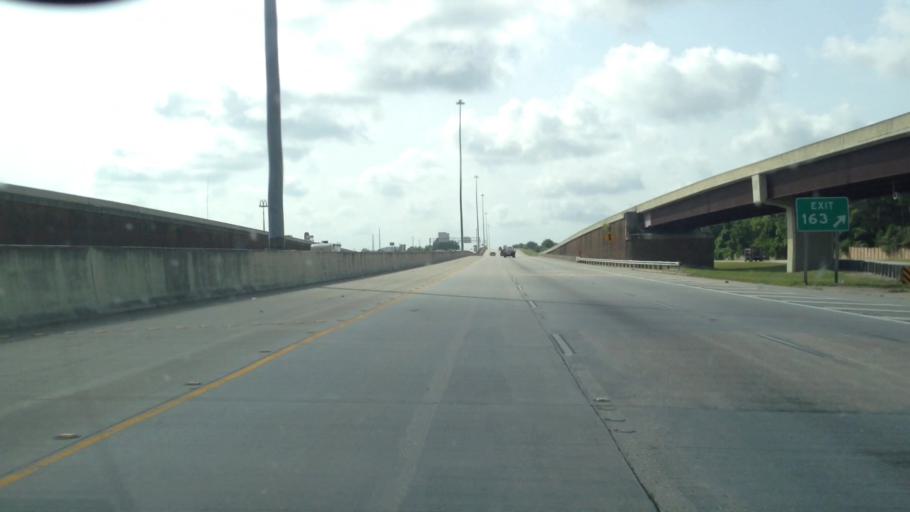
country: US
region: Louisiana
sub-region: East Baton Rouge Parish
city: Inniswold
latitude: 30.3865
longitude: -91.0726
